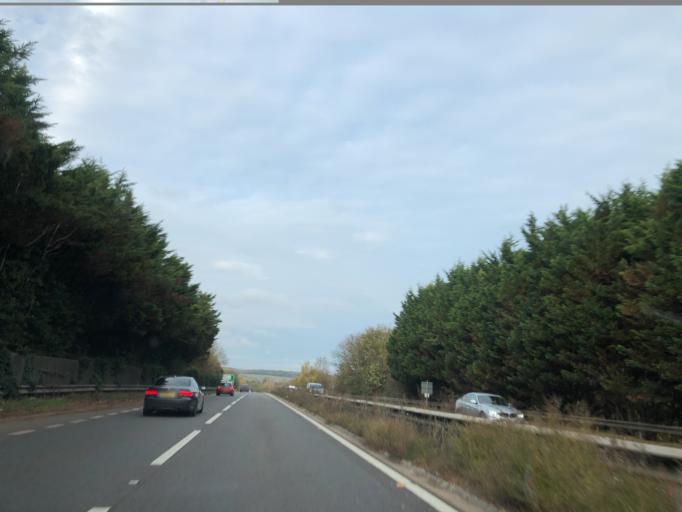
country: GB
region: England
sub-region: Buckinghamshire
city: Marlow
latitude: 51.5689
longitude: -0.7602
